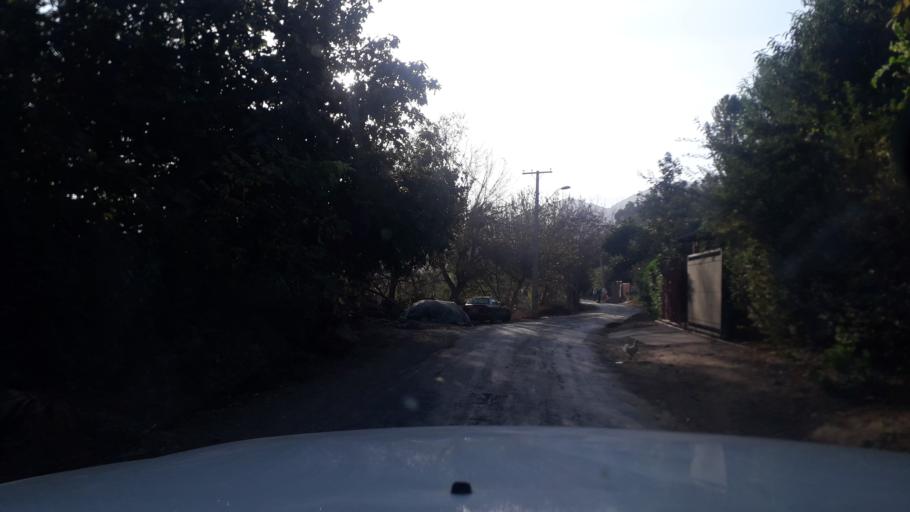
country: CL
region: Valparaiso
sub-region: Provincia de San Felipe
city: Llaillay
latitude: -32.8183
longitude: -71.0286
